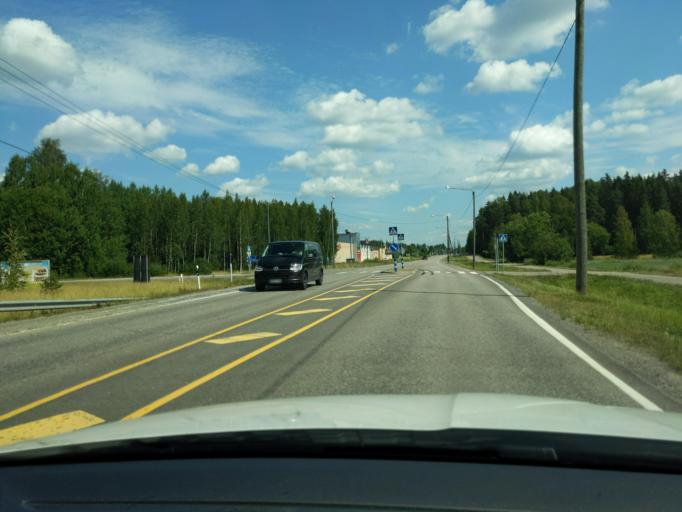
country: FI
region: Uusimaa
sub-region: Helsinki
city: Maentsaelae
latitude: 60.6212
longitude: 25.2842
